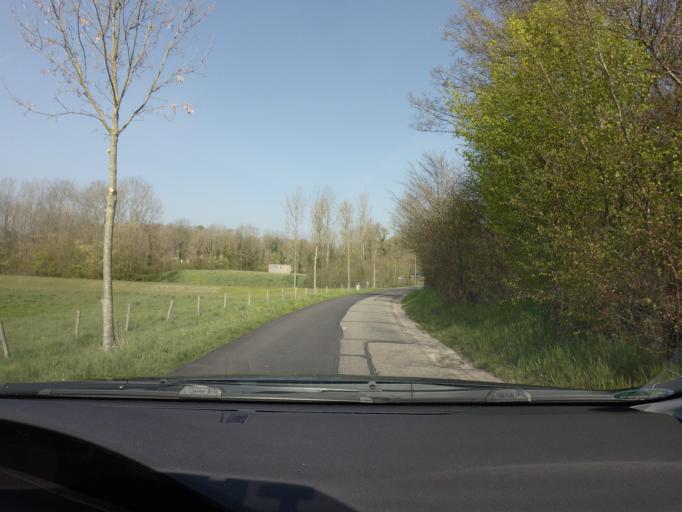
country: NL
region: Limburg
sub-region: Gemeente Meerssen
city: Meerssen
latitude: 50.8929
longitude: 5.7681
